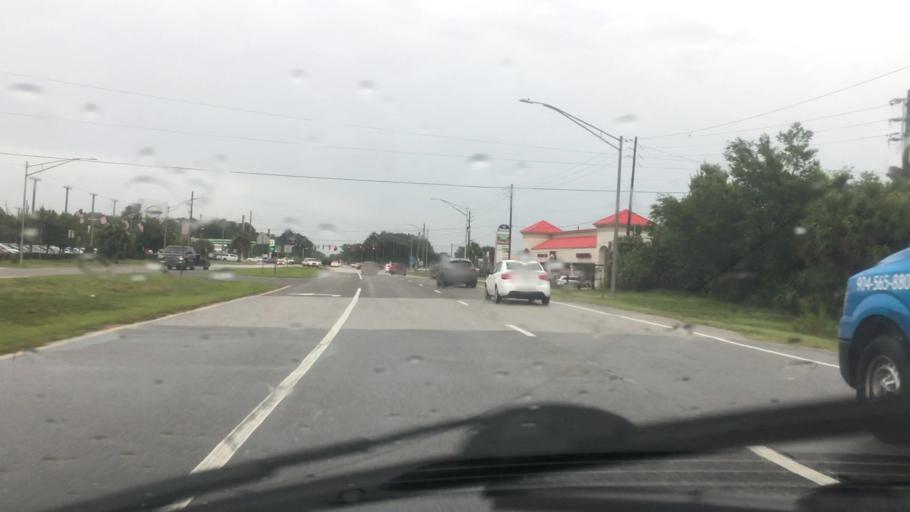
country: US
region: Florida
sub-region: Duval County
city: Atlantic Beach
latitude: 30.3221
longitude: -81.5230
